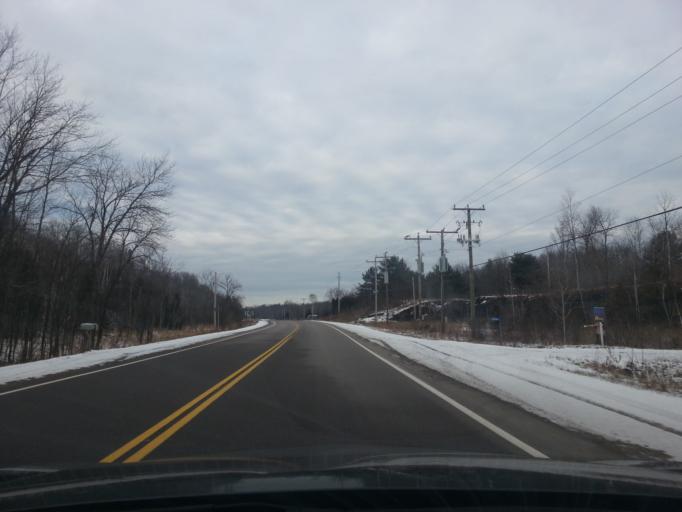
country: CA
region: Ontario
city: Skatepark
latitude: 44.7385
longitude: -76.9372
